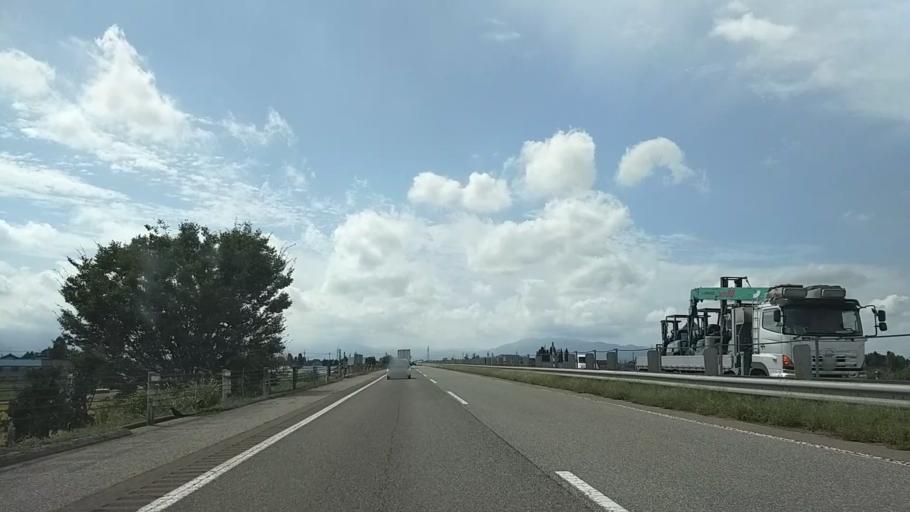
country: JP
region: Toyama
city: Nanto-shi
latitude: 36.6410
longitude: 136.9749
